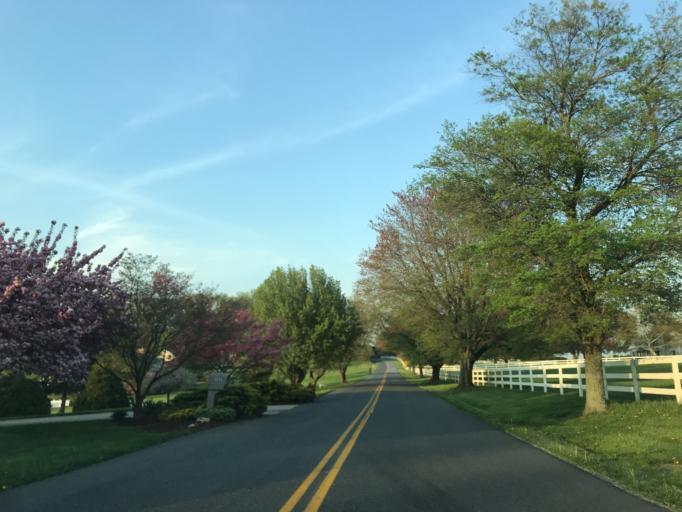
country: US
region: Maryland
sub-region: Harford County
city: Jarrettsville
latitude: 39.6188
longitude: -76.4865
